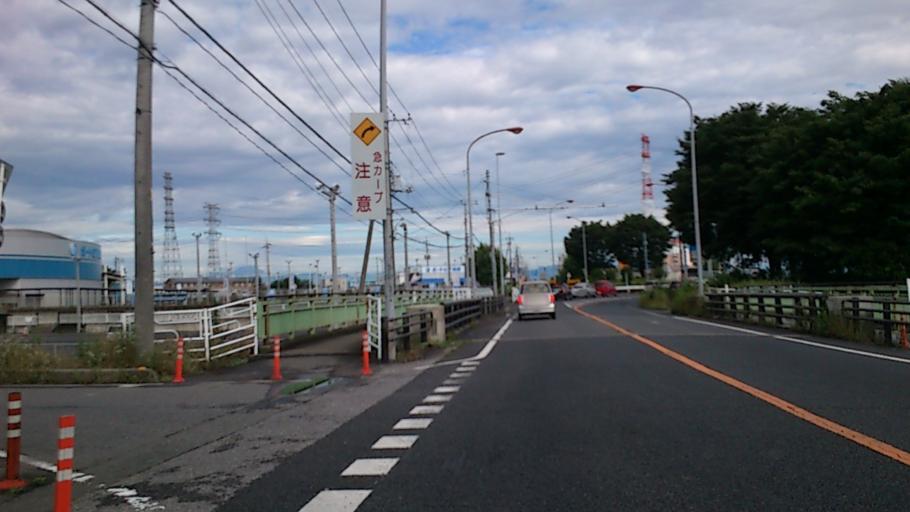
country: JP
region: Saitama
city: Honjo
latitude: 36.2224
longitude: 139.2275
